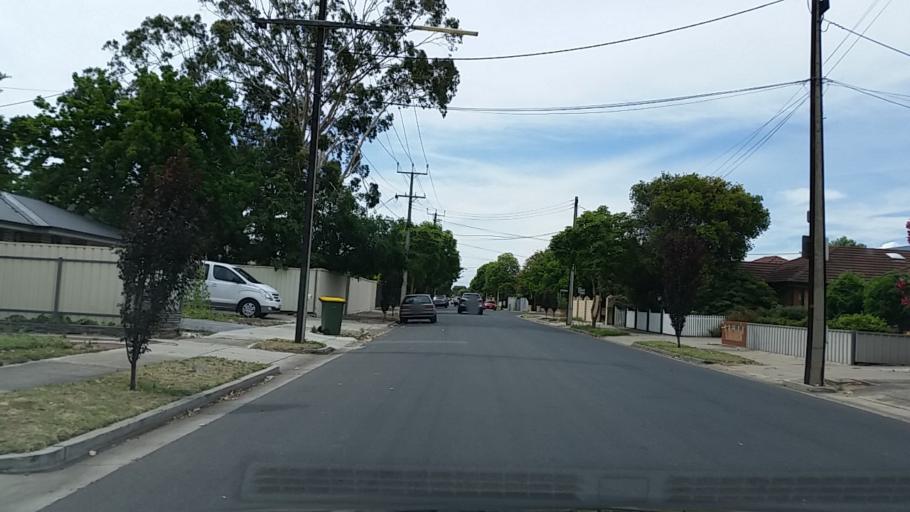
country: AU
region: South Australia
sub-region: City of West Torrens
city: Plympton
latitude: -34.9577
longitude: 138.5455
